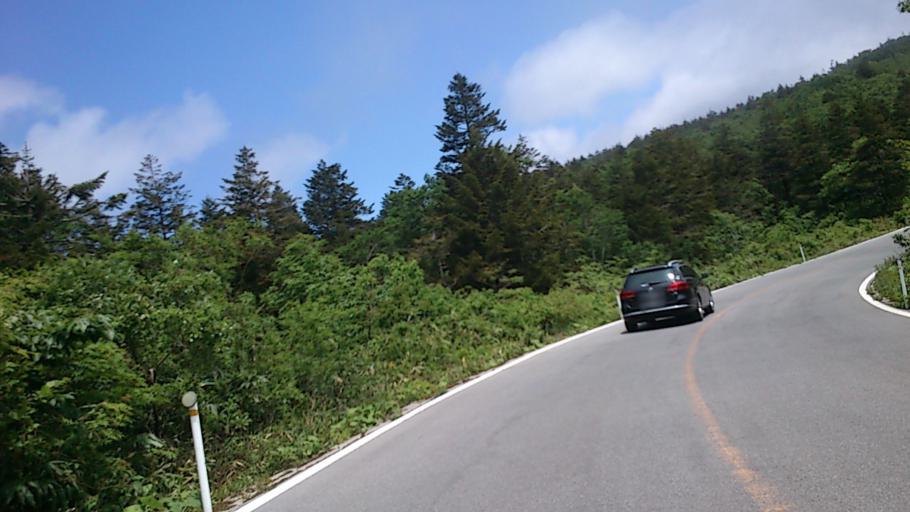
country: JP
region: Yamagata
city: Yamagata-shi
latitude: 38.1195
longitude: 140.4205
